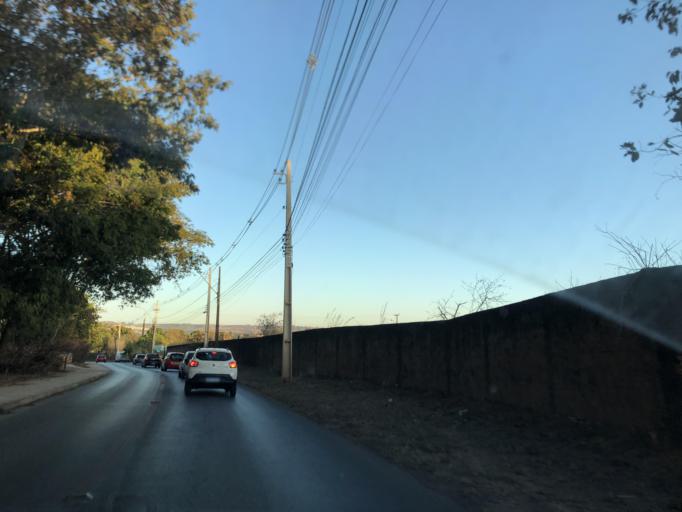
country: BR
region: Federal District
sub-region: Brasilia
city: Brasilia
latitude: -15.8771
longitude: -47.7803
